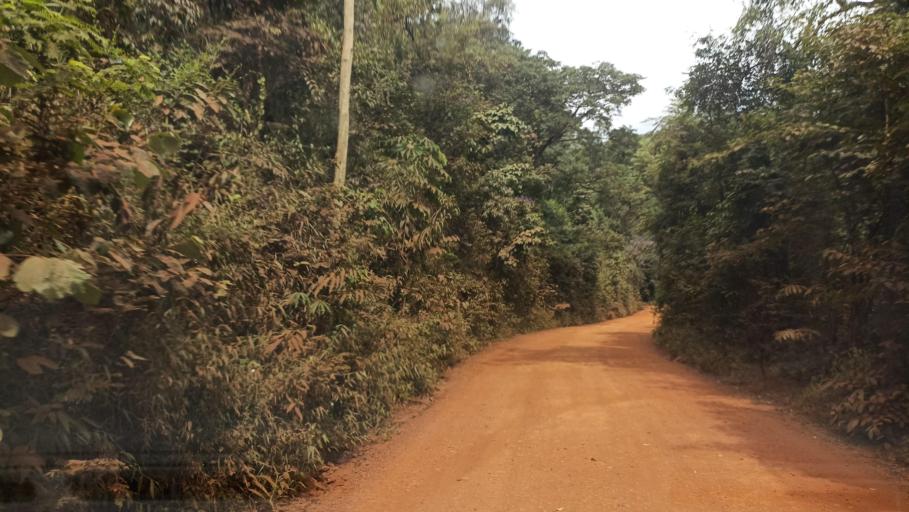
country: BR
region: Minas Gerais
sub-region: Itabirito
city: Itabirito
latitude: -20.3864
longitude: -43.7600
